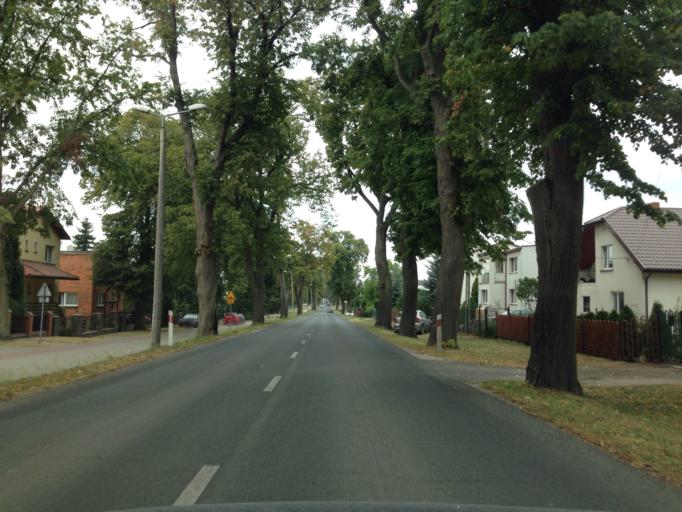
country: PL
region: Kujawsko-Pomorskie
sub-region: Powiat golubsko-dobrzynski
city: Kowalewo Pomorskie
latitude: 53.1563
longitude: 18.8905
